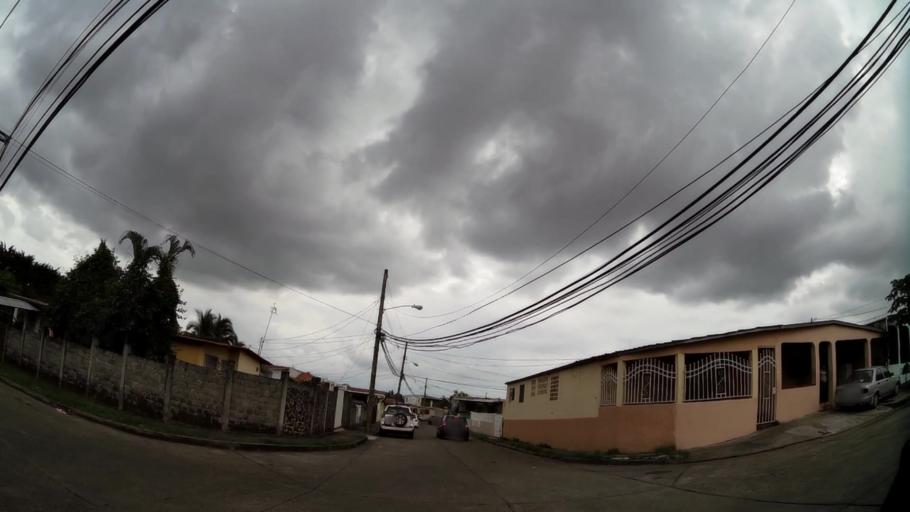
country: PA
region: Panama
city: Tocumen
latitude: 9.0611
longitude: -79.4168
